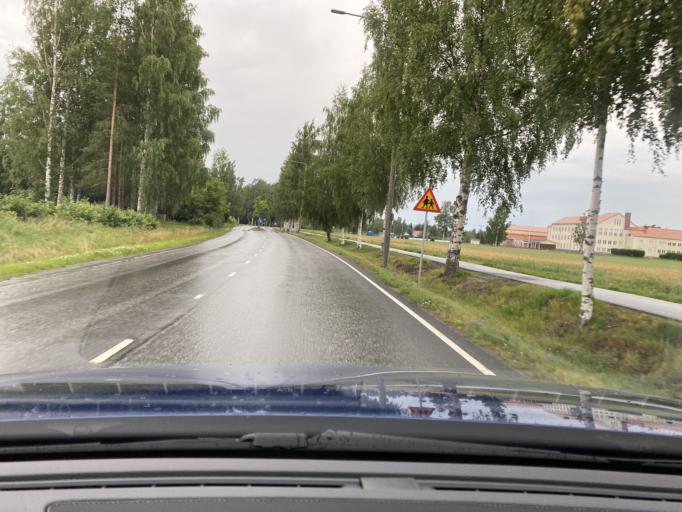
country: FI
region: Ostrobothnia
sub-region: Kyroenmaa
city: Laihia
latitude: 62.9777
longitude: 22.0018
